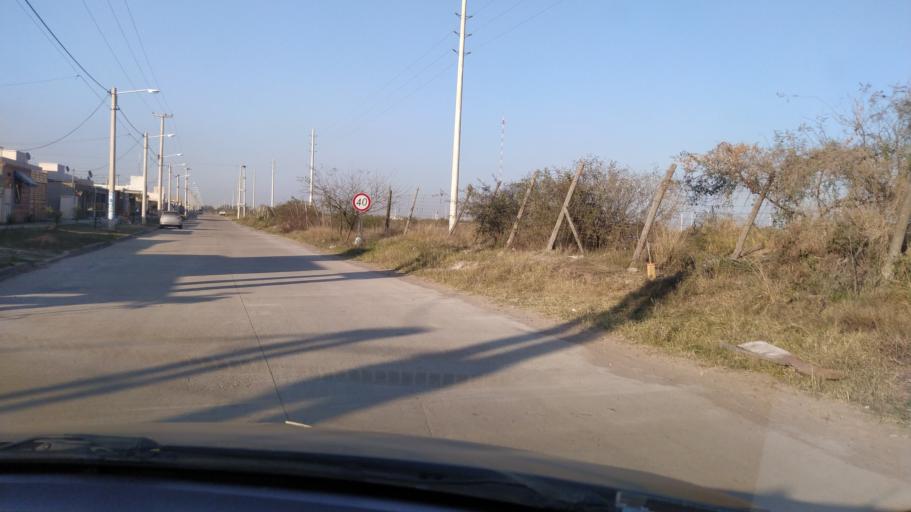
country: AR
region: Corrientes
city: Corrientes
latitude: -27.5221
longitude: -58.8073
